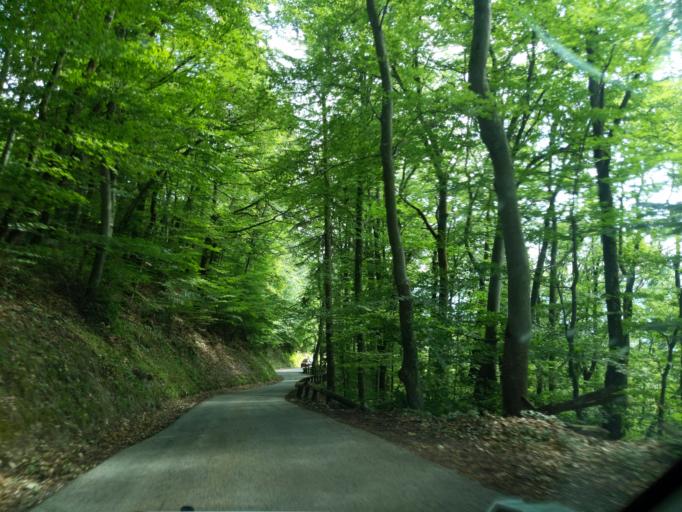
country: FR
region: Rhone-Alpes
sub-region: Departement de la Savoie
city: Ugine
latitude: 45.7425
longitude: 6.4370
